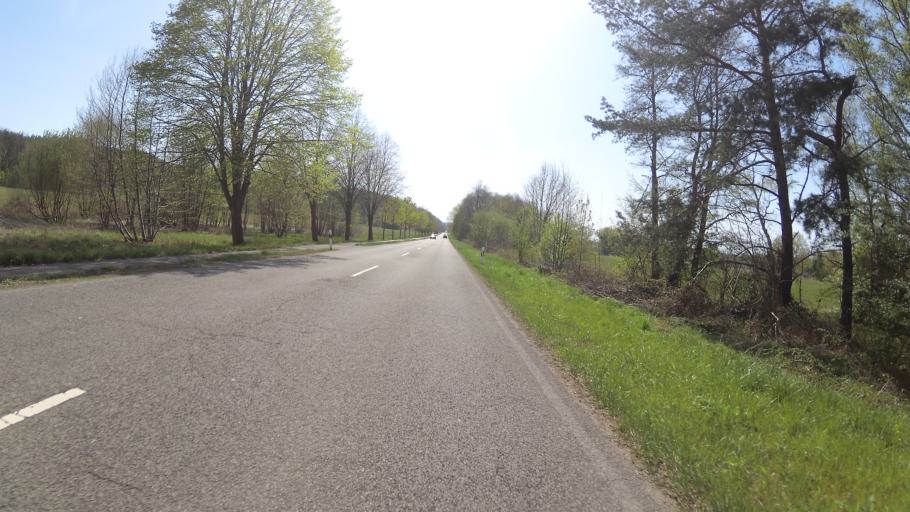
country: DE
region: Saarland
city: Homburg
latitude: 49.3315
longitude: 7.3632
